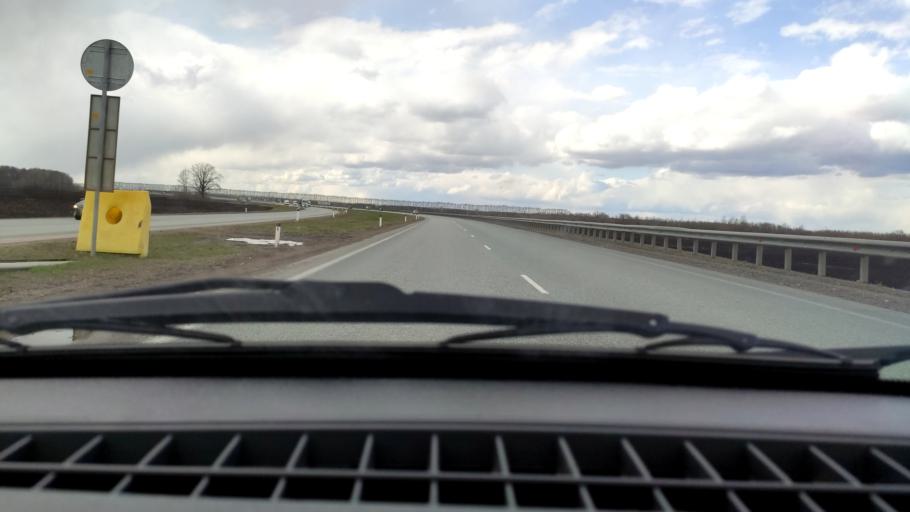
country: RU
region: Bashkortostan
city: Asanovo
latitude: 54.9774
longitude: 55.5686
